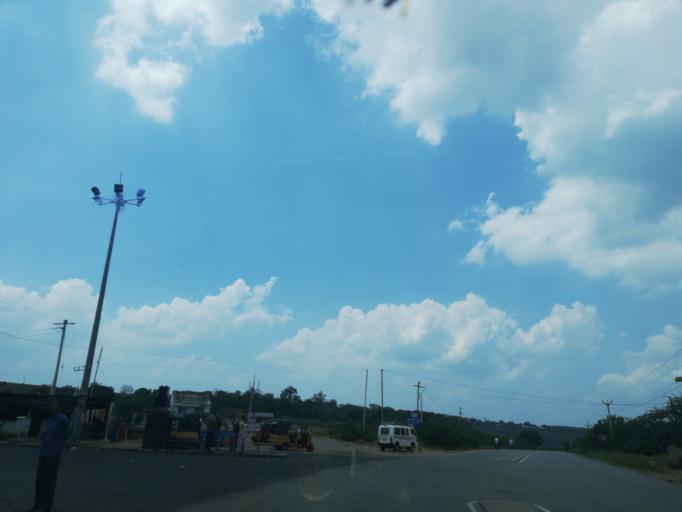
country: IN
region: Andhra Pradesh
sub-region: Guntur
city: Macherla
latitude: 16.5923
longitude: 79.3159
